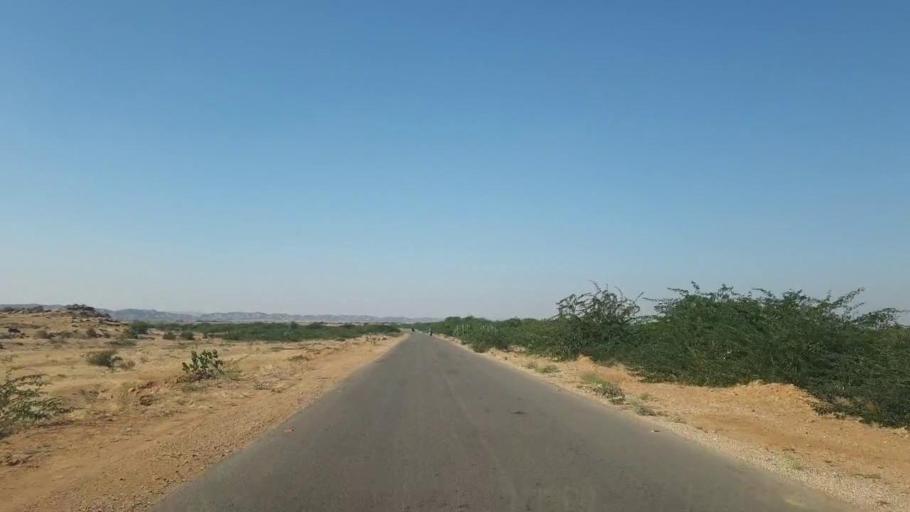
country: PK
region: Sindh
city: Malir Cantonment
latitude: 25.2740
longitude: 67.5902
